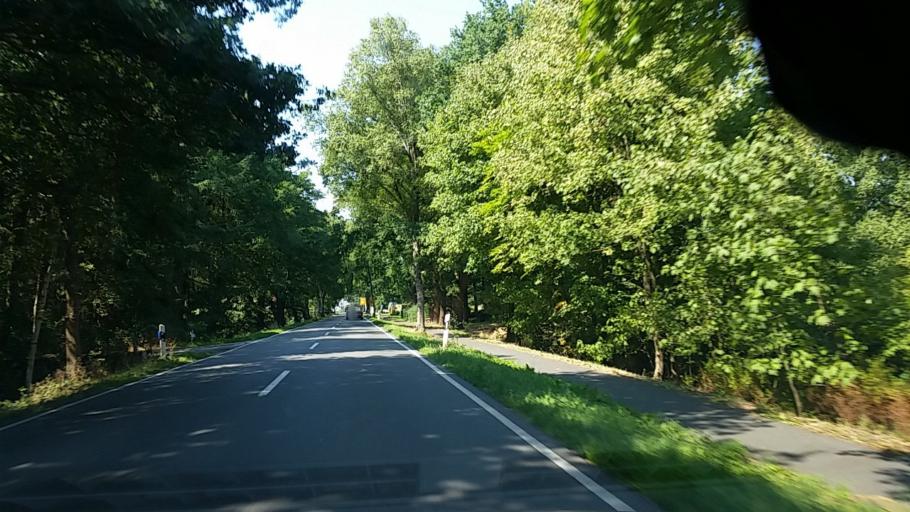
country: DE
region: Lower Saxony
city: Hellwege
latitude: 53.0532
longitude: 9.1743
